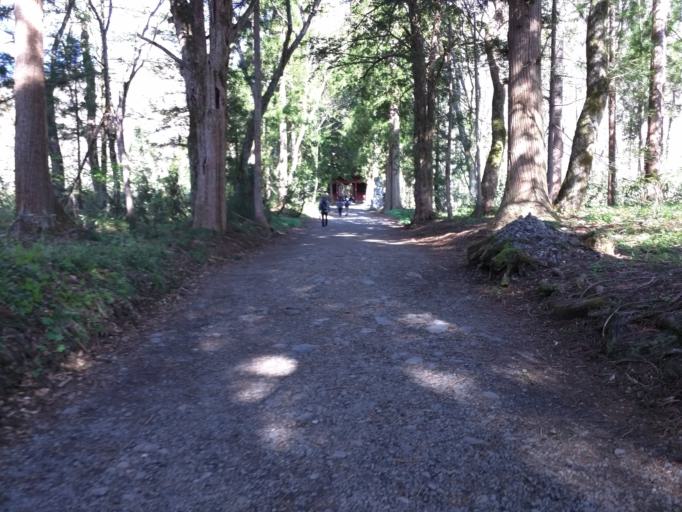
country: JP
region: Nagano
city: Nagano-shi
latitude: 36.7606
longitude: 138.0702
